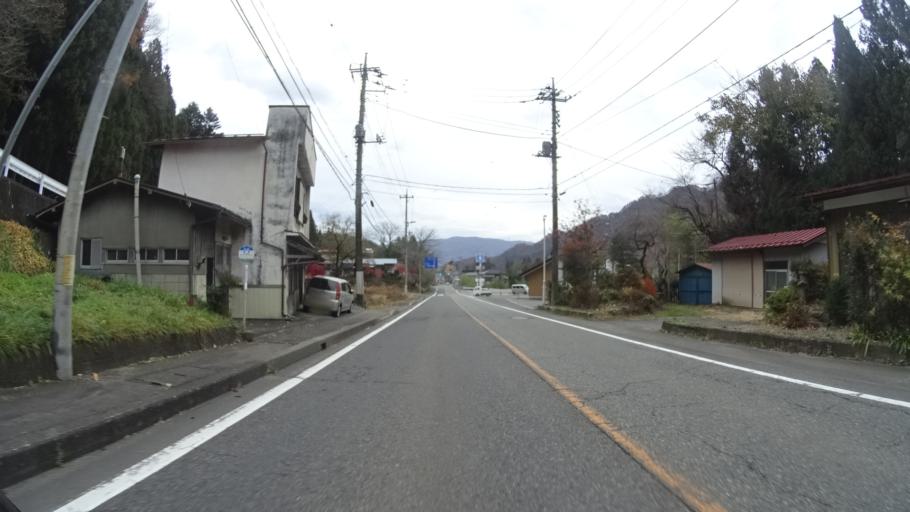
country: JP
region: Gunma
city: Nakanojomachi
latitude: 36.7242
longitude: 138.8941
